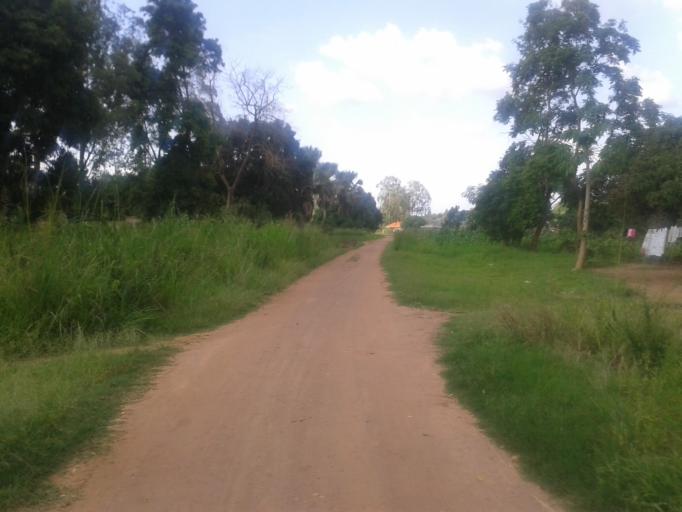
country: UG
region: Northern Region
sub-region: Gulu District
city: Gulu
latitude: 2.7930
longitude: 32.3060
